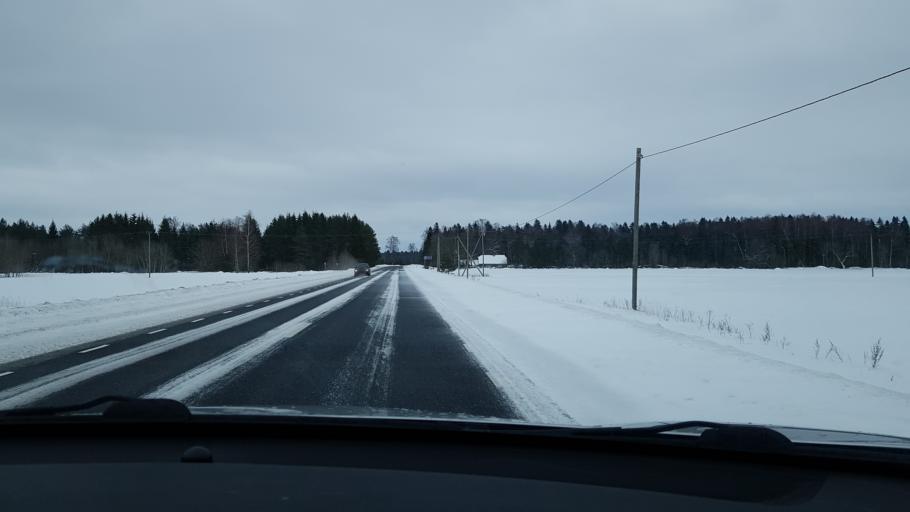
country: EE
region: Jaervamaa
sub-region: Jaerva-Jaani vald
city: Jarva-Jaani
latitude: 59.1070
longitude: 25.8051
